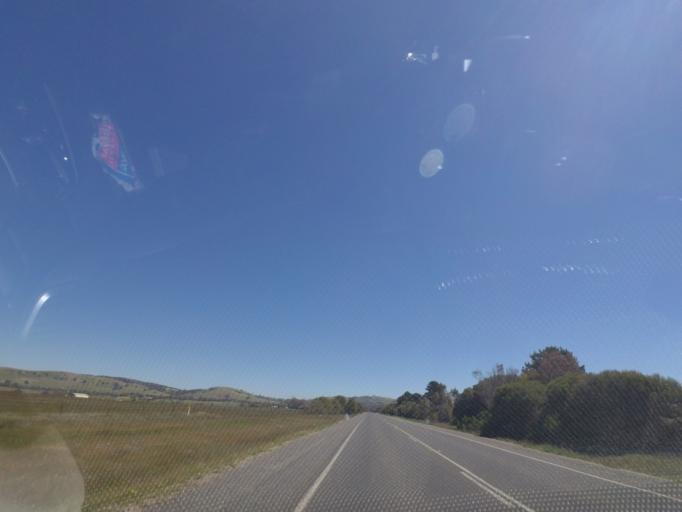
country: AU
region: Victoria
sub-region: Hume
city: Sunbury
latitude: -37.3082
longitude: 144.8411
